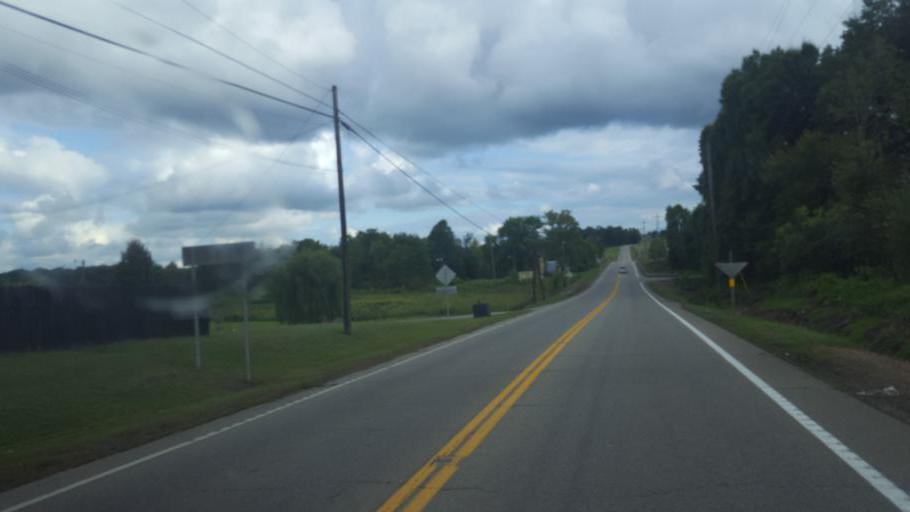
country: US
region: Ohio
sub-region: Jackson County
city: Oak Hill
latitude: 38.9336
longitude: -82.5668
